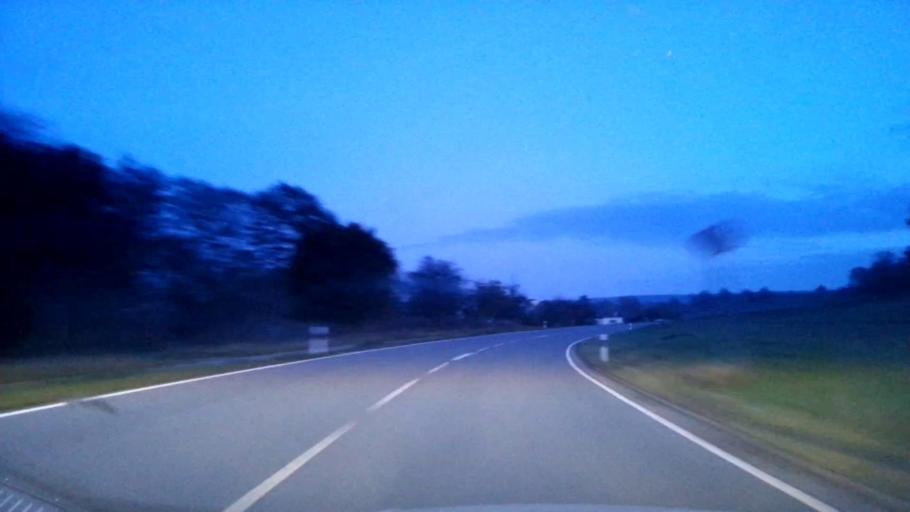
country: DE
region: Bavaria
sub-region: Upper Franconia
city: Pettstadt
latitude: 49.8402
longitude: 10.9244
